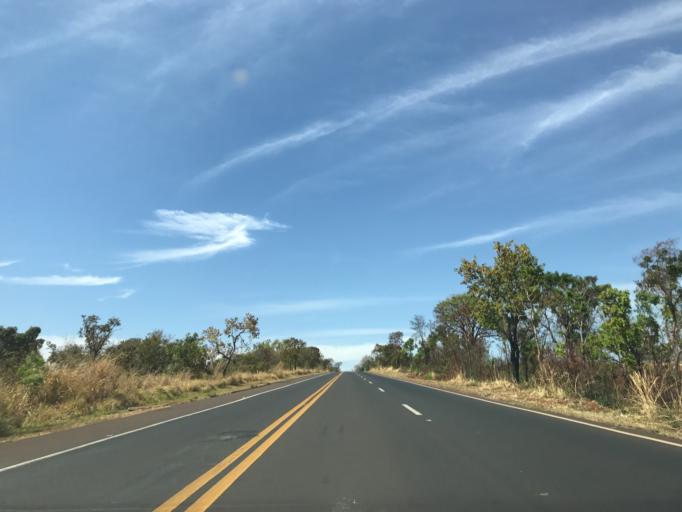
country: BR
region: Minas Gerais
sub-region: Monte Alegre De Minas
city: Monte Alegre de Minas
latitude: -18.9689
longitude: -49.0253
